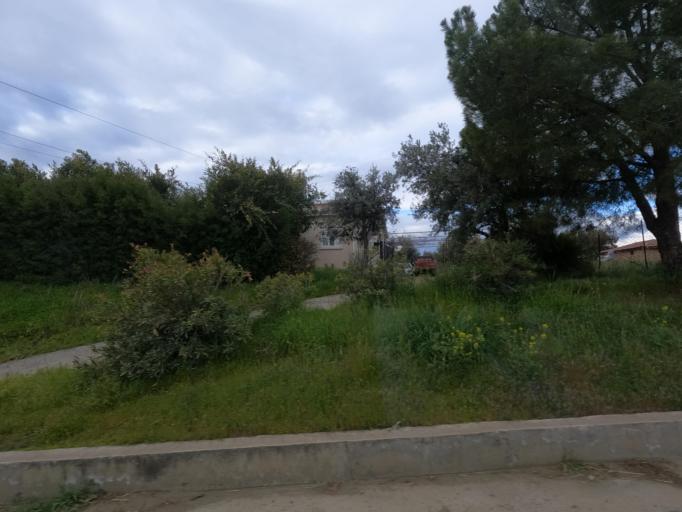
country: CY
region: Lefkosia
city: Lefka
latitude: 35.0803
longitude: 32.8938
